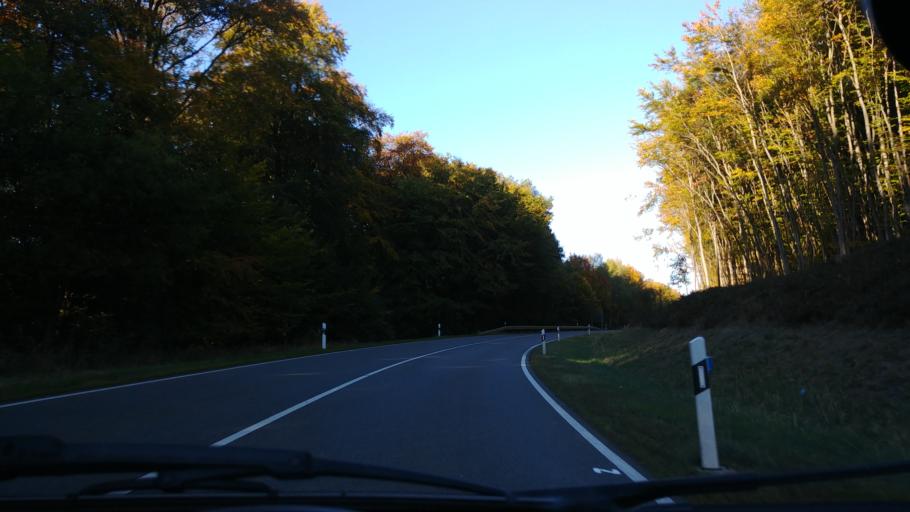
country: DE
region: Rheinland-Pfalz
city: Rettert
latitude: 50.2062
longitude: 7.9438
